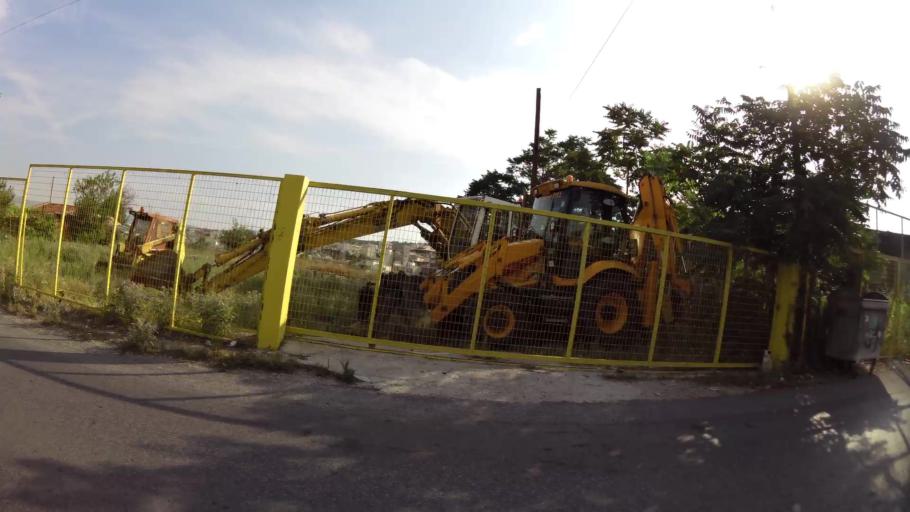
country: GR
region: Central Macedonia
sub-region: Nomos Thessalonikis
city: Sykies
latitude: 40.6566
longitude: 22.9520
